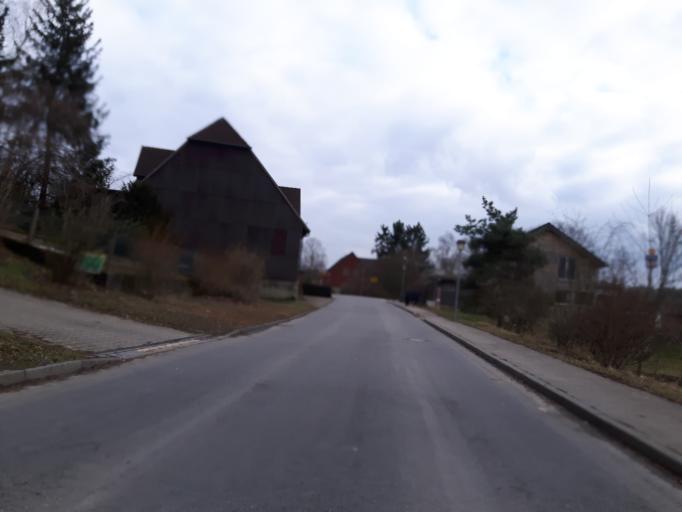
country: DE
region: Baden-Wuerttemberg
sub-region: Regierungsbezirk Stuttgart
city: Ohringen
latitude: 49.2107
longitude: 9.4802
